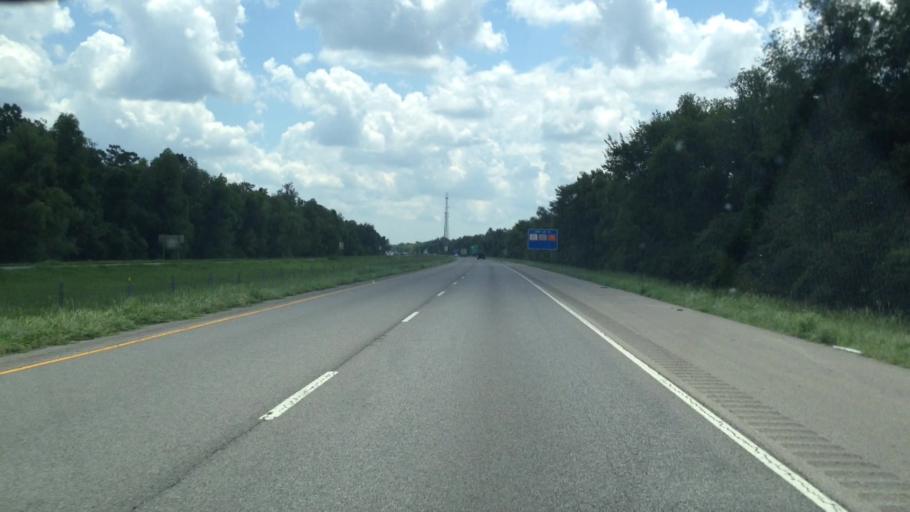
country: US
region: Louisiana
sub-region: Saint James Parish
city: Gramercy
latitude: 30.1257
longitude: -90.7000
